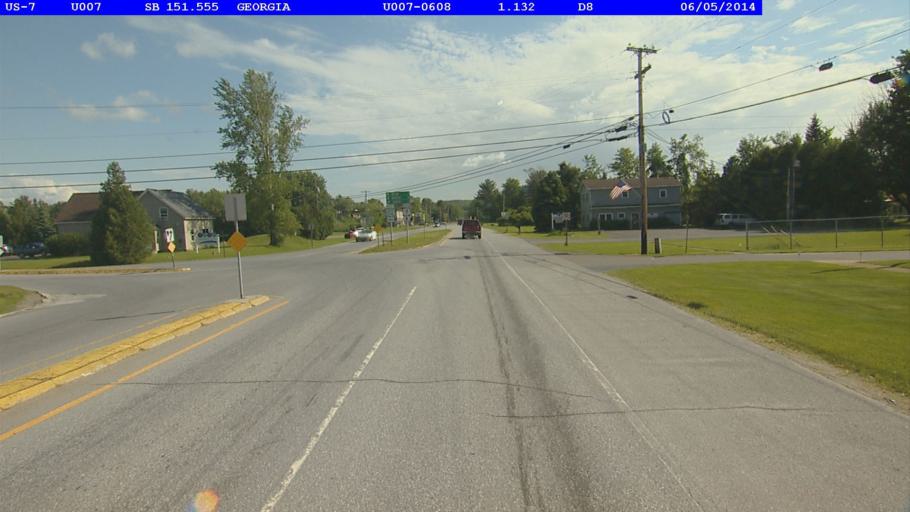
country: US
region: Vermont
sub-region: Chittenden County
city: Milton
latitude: 44.6952
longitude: -73.1077
